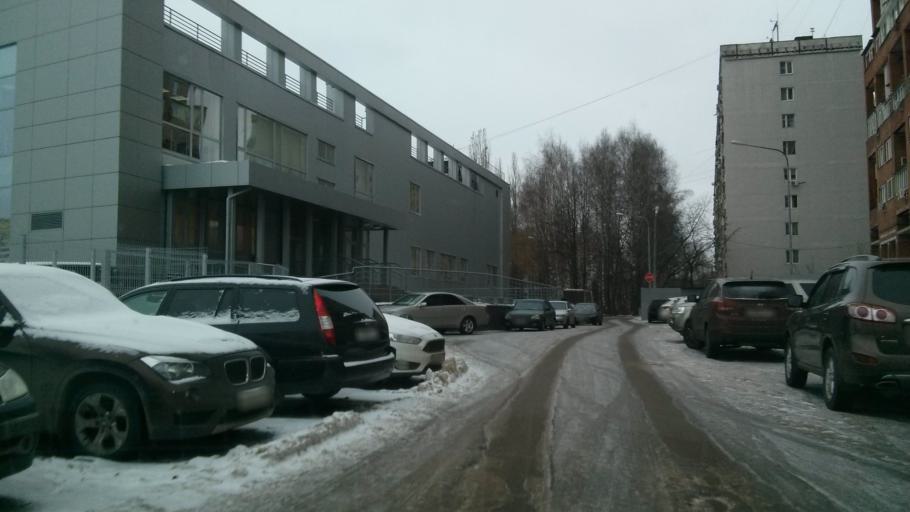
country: RU
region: Nizjnij Novgorod
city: Afonino
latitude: 56.2985
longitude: 44.0765
